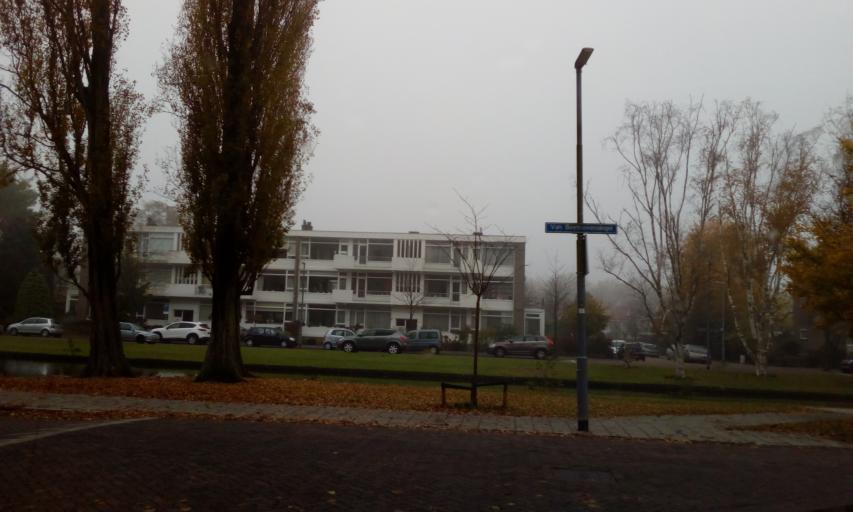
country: NL
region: South Holland
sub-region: Gemeente Lansingerland
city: Bergschenhoek
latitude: 51.9601
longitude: 4.5086
